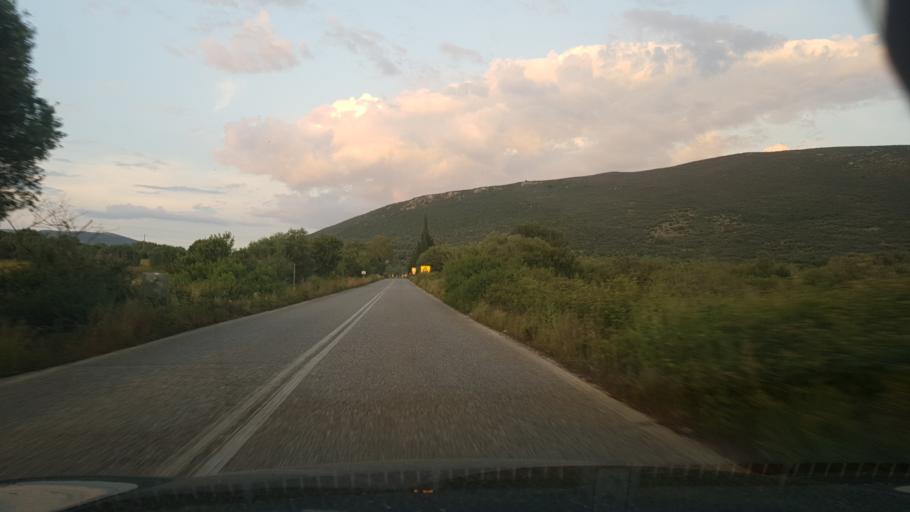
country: GR
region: West Greece
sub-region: Nomos Aitolias kai Akarnanias
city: Vonitsa
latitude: 38.8974
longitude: 20.8674
